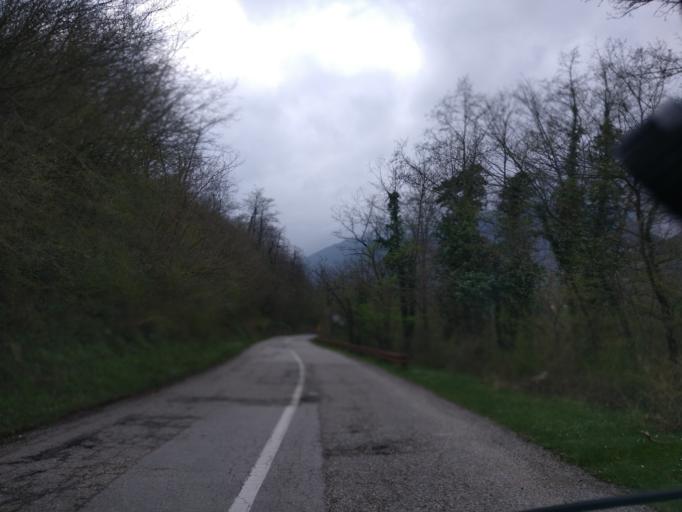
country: BA
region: Republika Srpska
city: Foca
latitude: 43.4679
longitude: 18.7473
